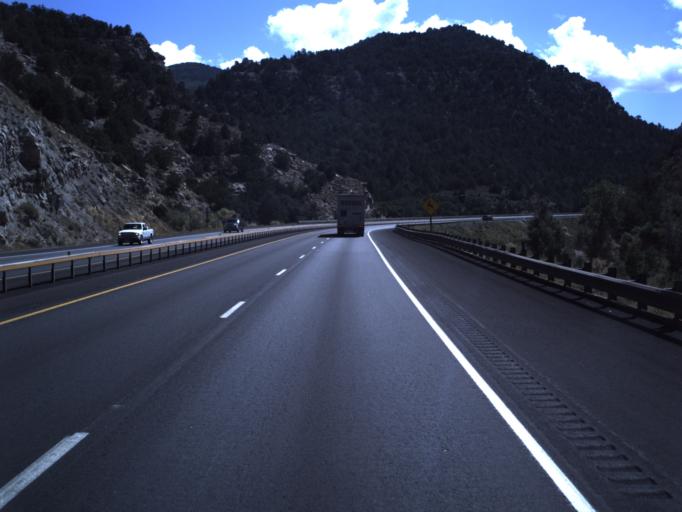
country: US
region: Utah
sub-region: Sevier County
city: Salina
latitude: 38.9050
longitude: -111.6367
